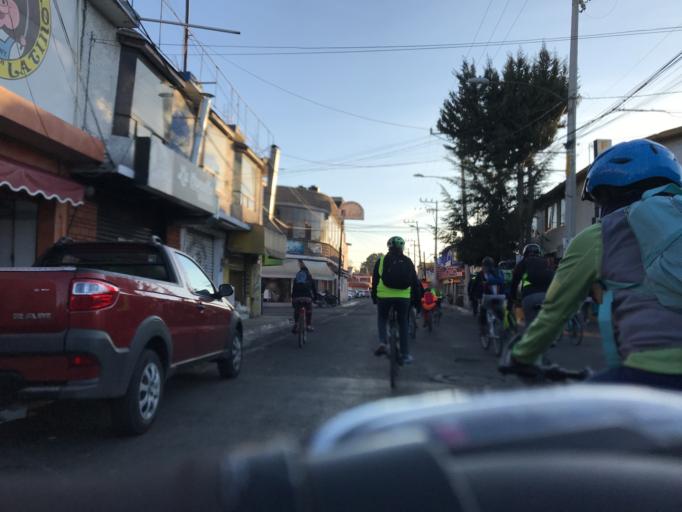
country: MX
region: Mexico
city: Cuautitlan Izcalli
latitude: 19.6595
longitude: -99.2134
